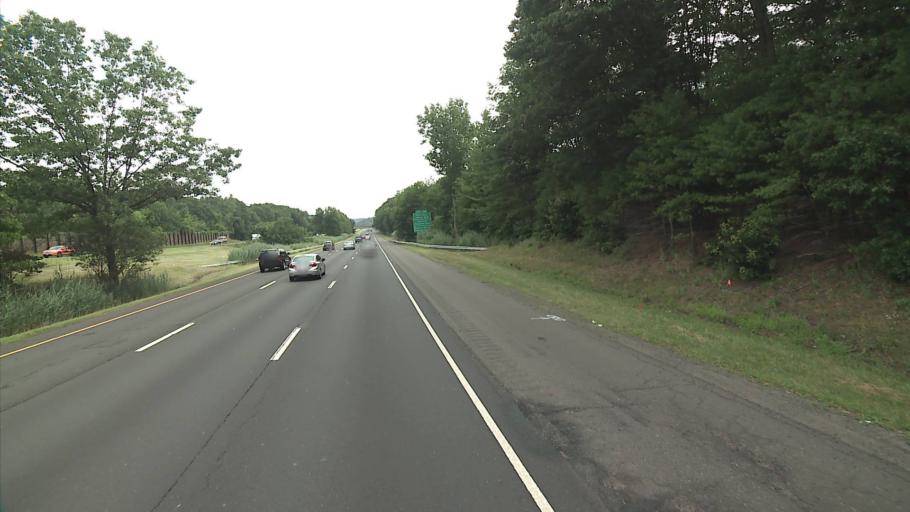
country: US
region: Connecticut
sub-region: Hartford County
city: Plainville
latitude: 41.6452
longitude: -72.8609
